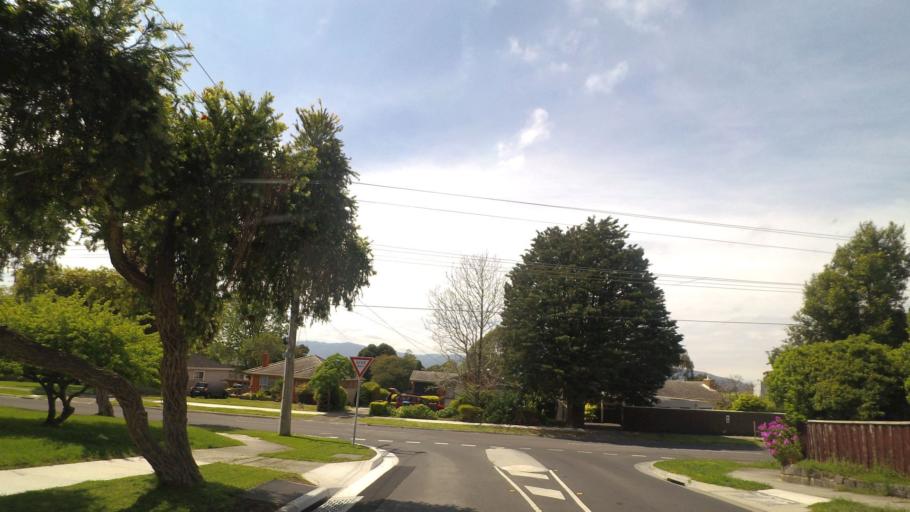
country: AU
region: Victoria
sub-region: Knox
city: Bayswater
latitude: -37.8491
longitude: 145.2543
